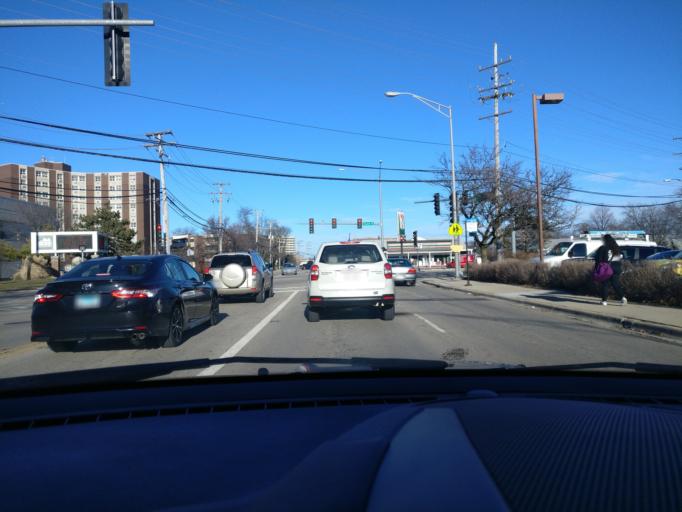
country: US
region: Illinois
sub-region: Cook County
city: Skokie
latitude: 42.0477
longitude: -87.7491
